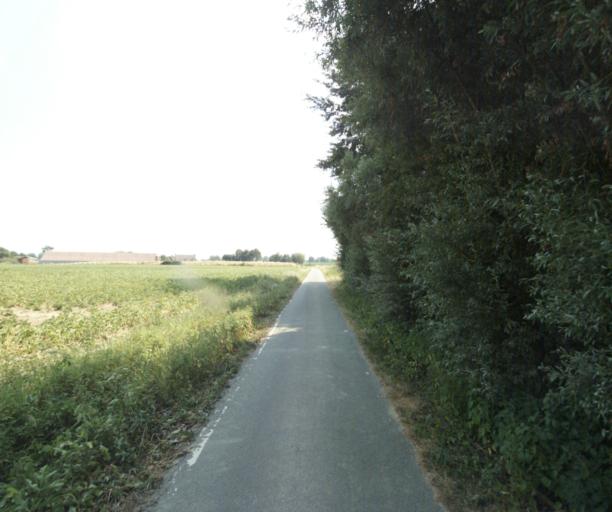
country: FR
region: Nord-Pas-de-Calais
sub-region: Departement du Nord
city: Quesnoy-sur-Deule
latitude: 50.7273
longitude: 3.0167
